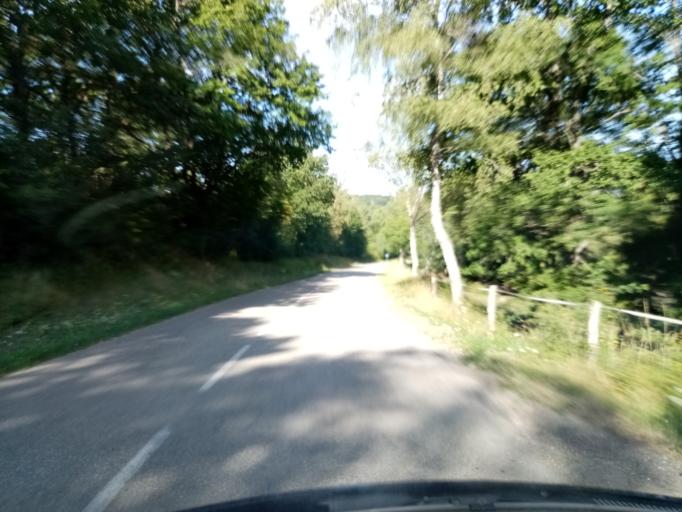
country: FR
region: Alsace
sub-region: Departement du Bas-Rhin
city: Ville
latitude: 48.3498
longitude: 7.3344
